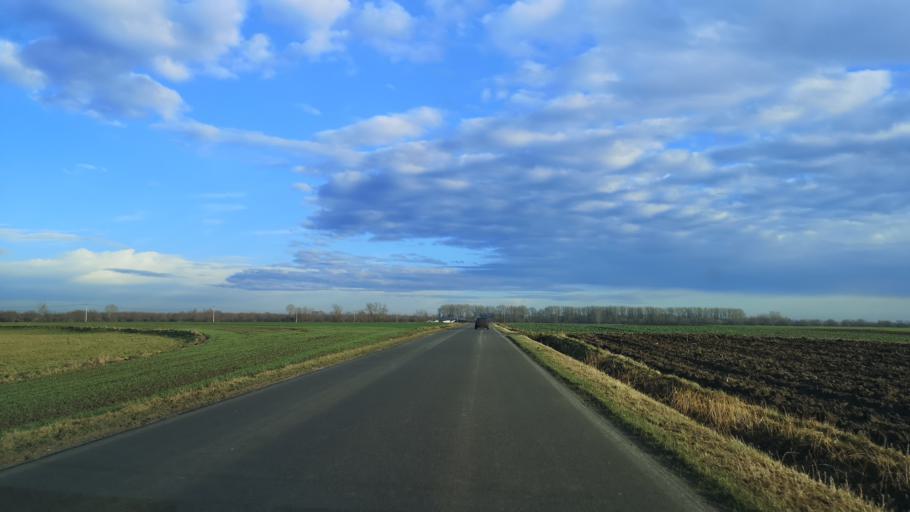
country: PL
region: Subcarpathian Voivodeship
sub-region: Powiat lezajski
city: Wierzawice
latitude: 50.2470
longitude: 22.4840
